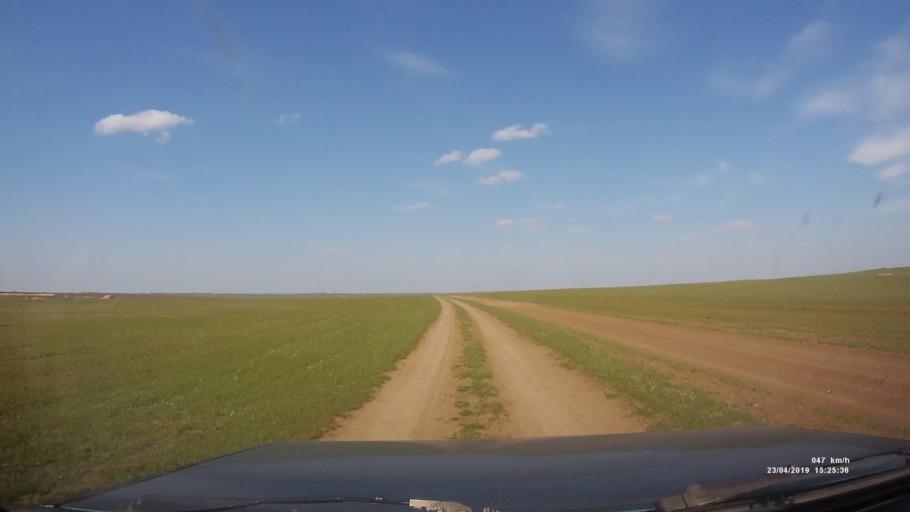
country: RU
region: Rostov
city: Remontnoye
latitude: 46.5425
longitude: 42.9833
